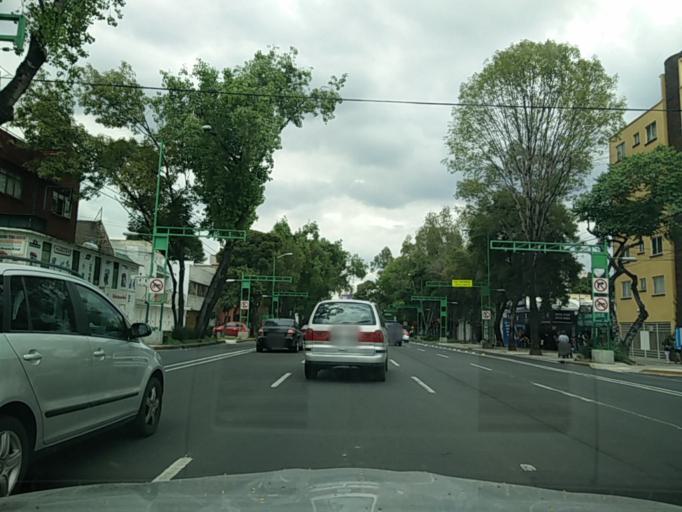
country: MX
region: Mexico City
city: Colonia Nativitas
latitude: 19.3799
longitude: -99.1480
